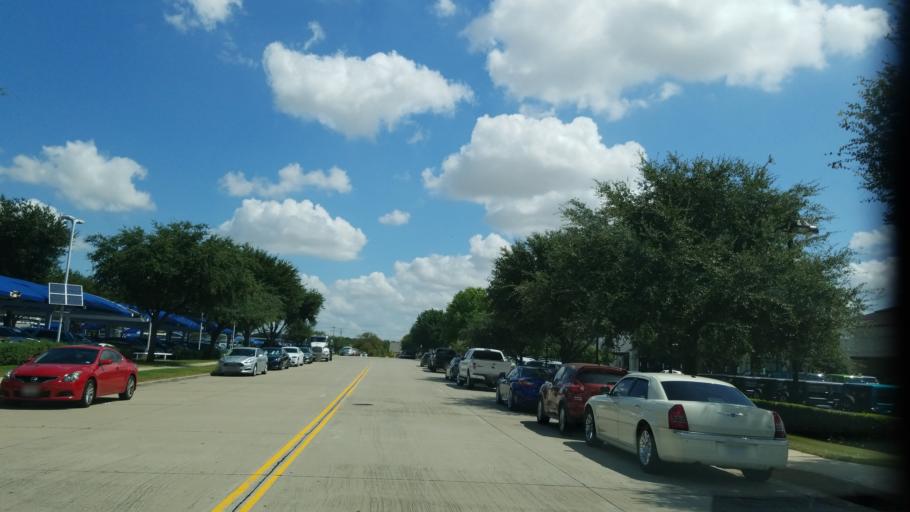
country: US
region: Texas
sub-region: Tarrant County
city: Grapevine
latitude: 32.9081
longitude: -97.0975
